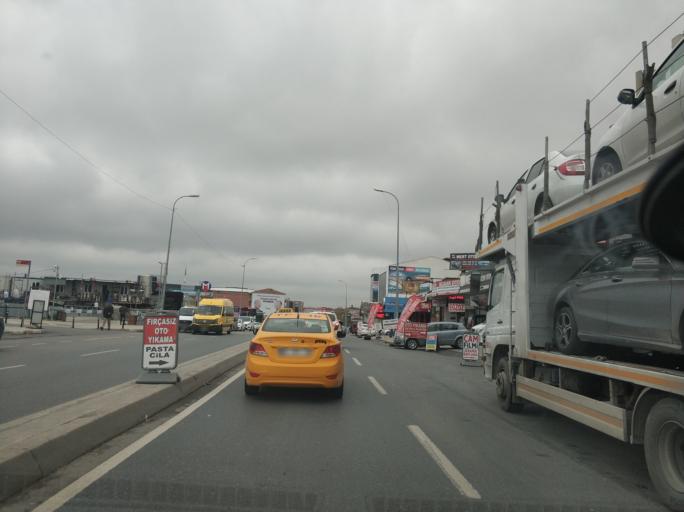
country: TR
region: Istanbul
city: Umraniye
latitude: 41.0202
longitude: 29.1294
